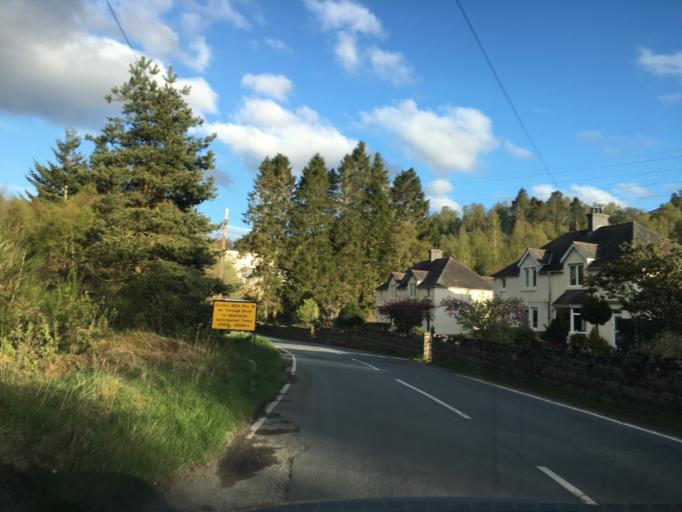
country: GB
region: Scotland
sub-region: Perth and Kinross
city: Aberfeldy
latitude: 56.7075
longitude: -4.0235
